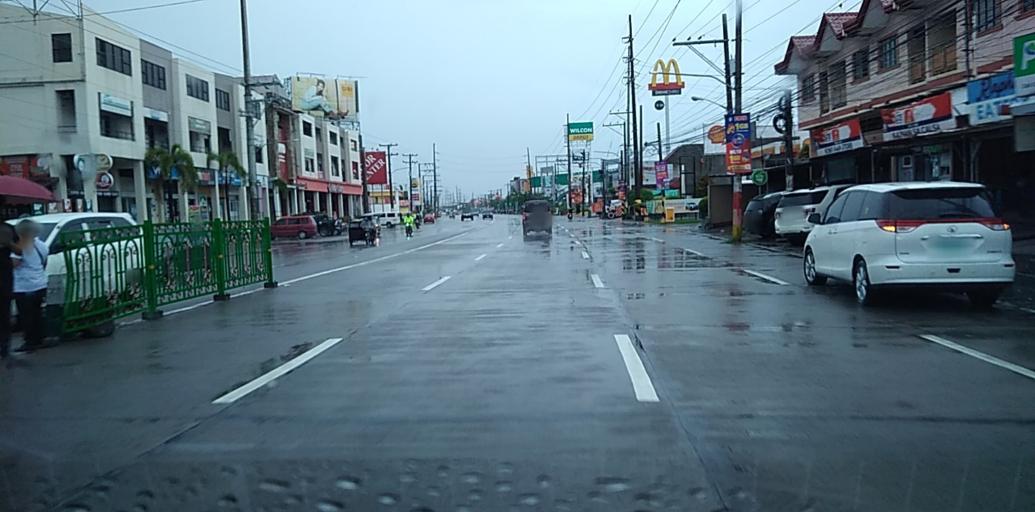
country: PH
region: Central Luzon
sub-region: Province of Pampanga
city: Del Pilar
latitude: 15.0513
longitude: 120.7028
